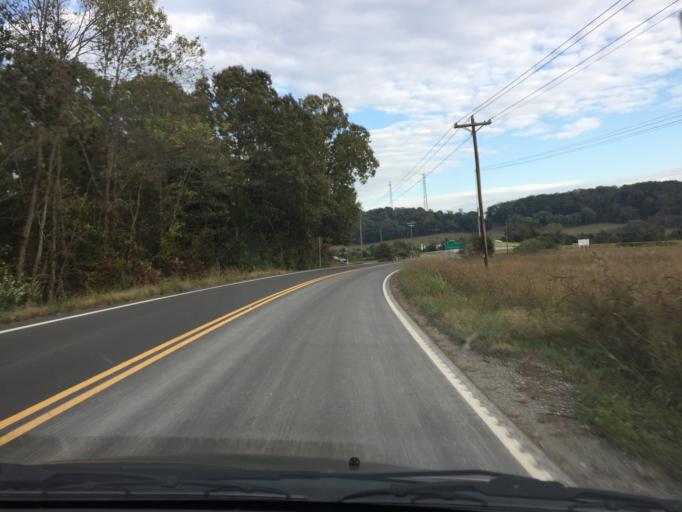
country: US
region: Tennessee
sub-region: Monroe County
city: Sweetwater
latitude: 35.6246
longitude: -84.4956
